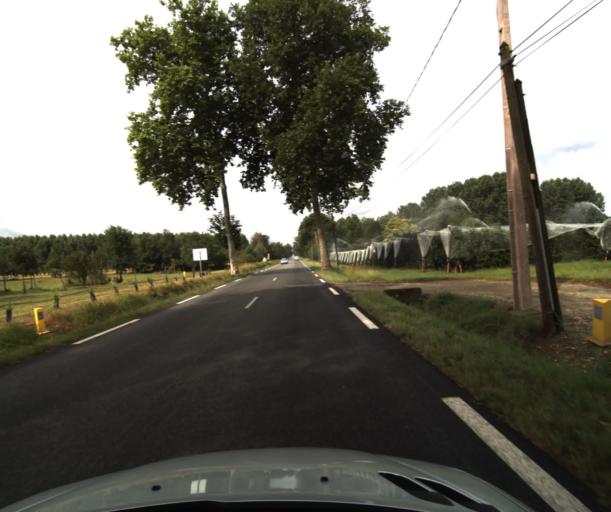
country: FR
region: Midi-Pyrenees
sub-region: Departement du Tarn-et-Garonne
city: Castelsarrasin
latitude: 44.0327
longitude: 1.0999
